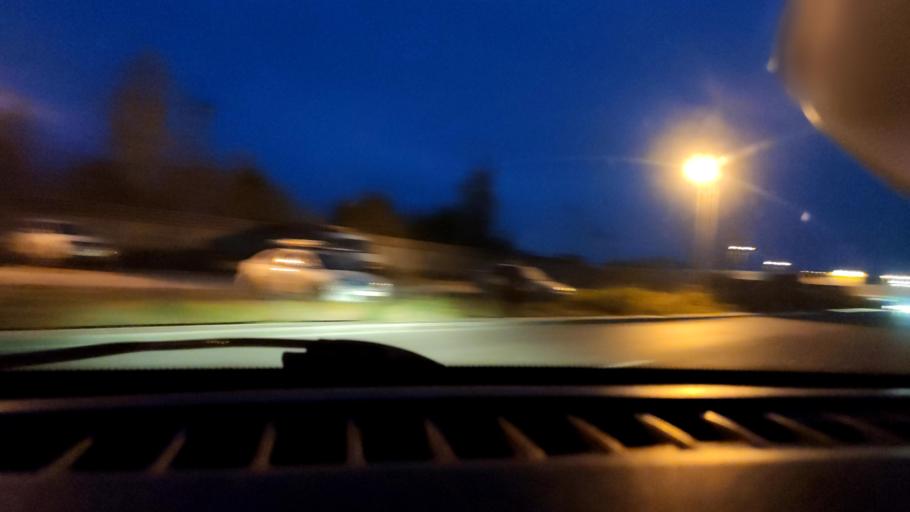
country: RU
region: Samara
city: Samara
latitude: 53.2108
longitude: 50.1935
